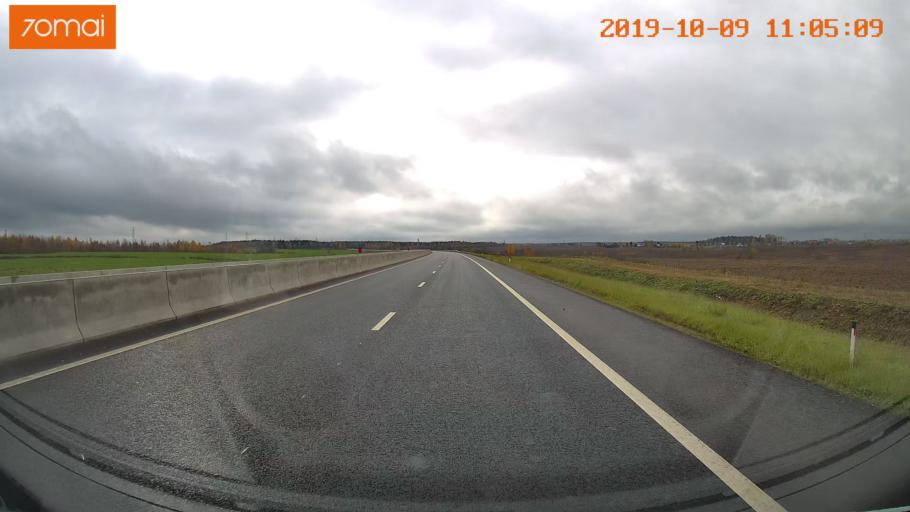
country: RU
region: Vologda
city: Molochnoye
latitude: 59.2036
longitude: 39.7600
